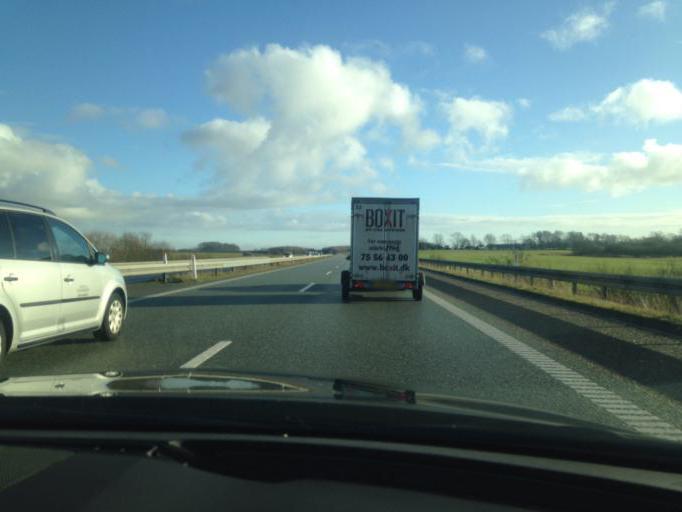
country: DK
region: South Denmark
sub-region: Vejen Kommune
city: Brorup
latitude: 55.5062
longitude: 9.0073
